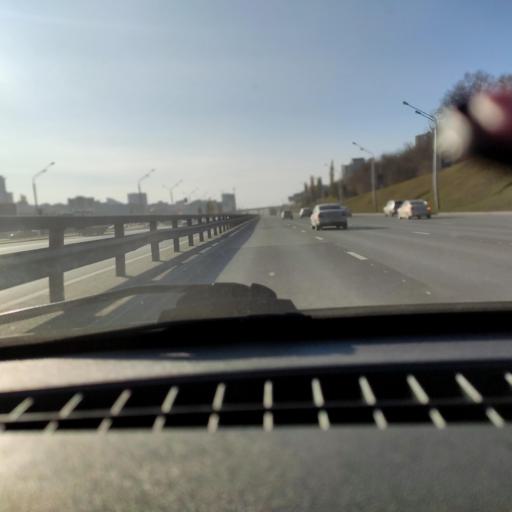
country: RU
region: Bashkortostan
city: Ufa
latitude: 54.7288
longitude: 55.9930
